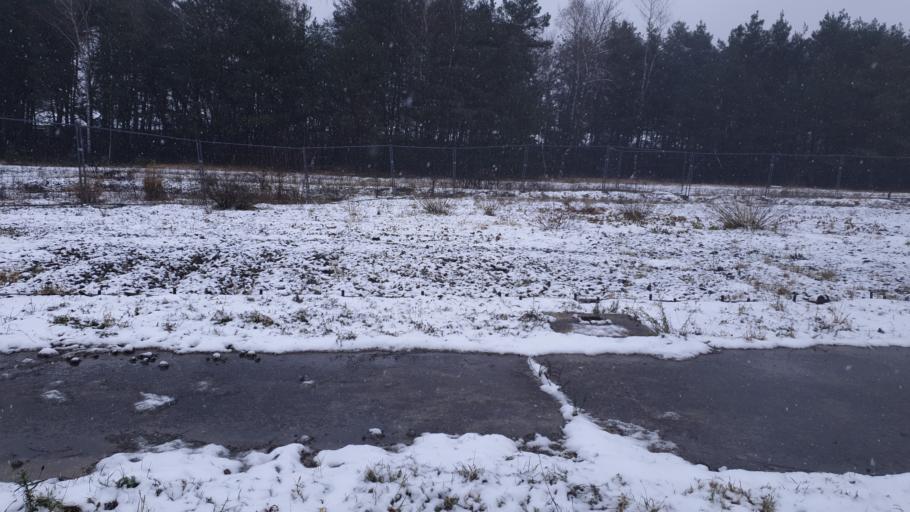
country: DE
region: Bavaria
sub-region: Upper Bavaria
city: Grafelfing
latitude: 48.1352
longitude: 11.4223
